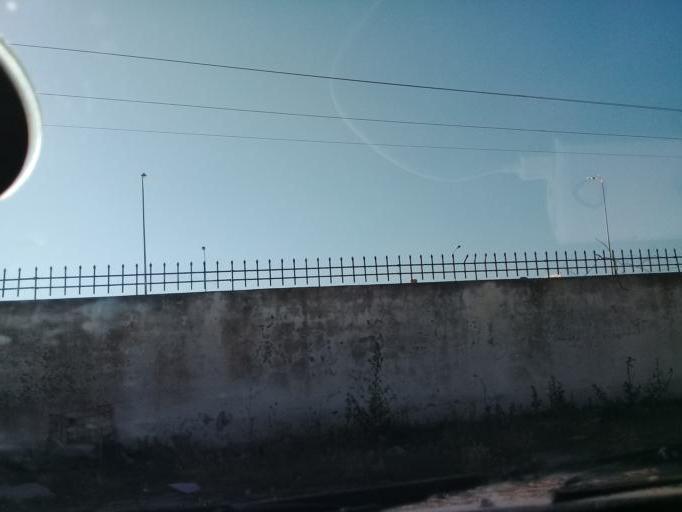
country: TN
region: Tunis
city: La Goulette
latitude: 36.8249
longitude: 10.3081
